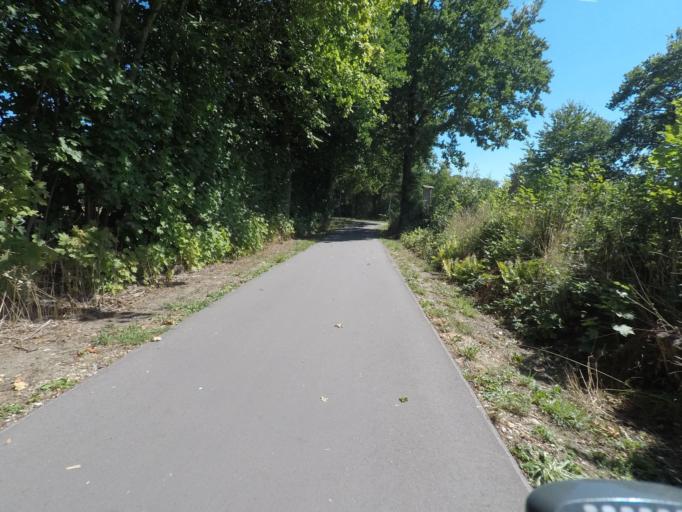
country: DE
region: Schleswig-Holstein
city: Gronwohld
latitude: 53.6354
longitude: 10.3834
